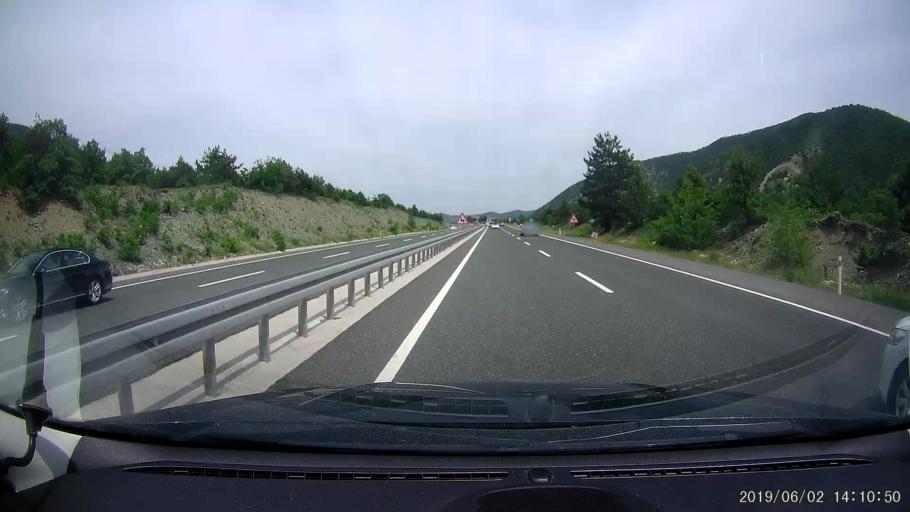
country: TR
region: Cankiri
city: Yaprakli
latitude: 40.9049
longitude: 33.7719
